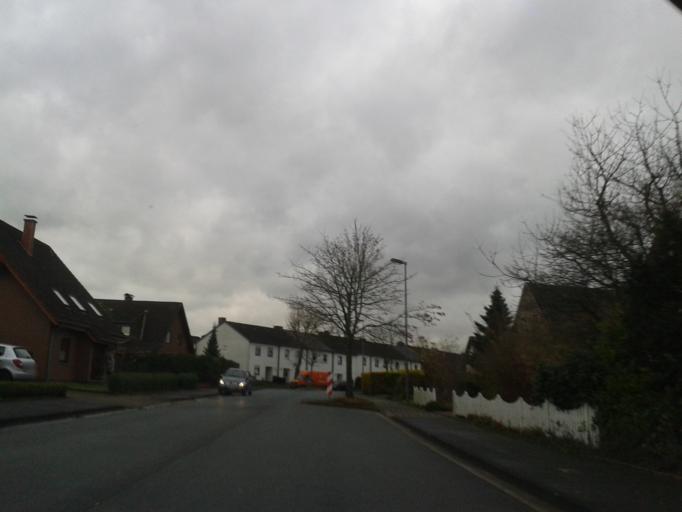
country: DE
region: North Rhine-Westphalia
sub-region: Regierungsbezirk Detmold
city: Blomberg
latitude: 51.9408
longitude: 9.1048
